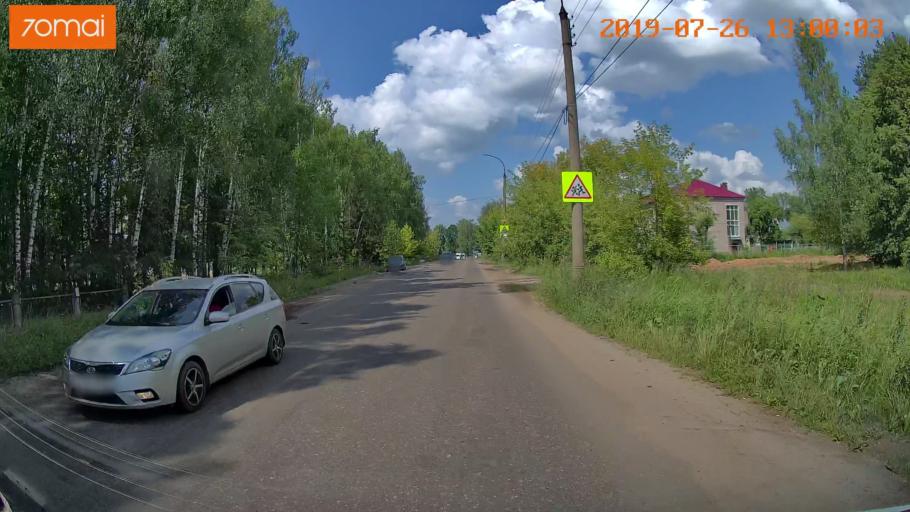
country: RU
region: Ivanovo
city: Bogorodskoye
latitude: 57.0318
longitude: 41.0183
